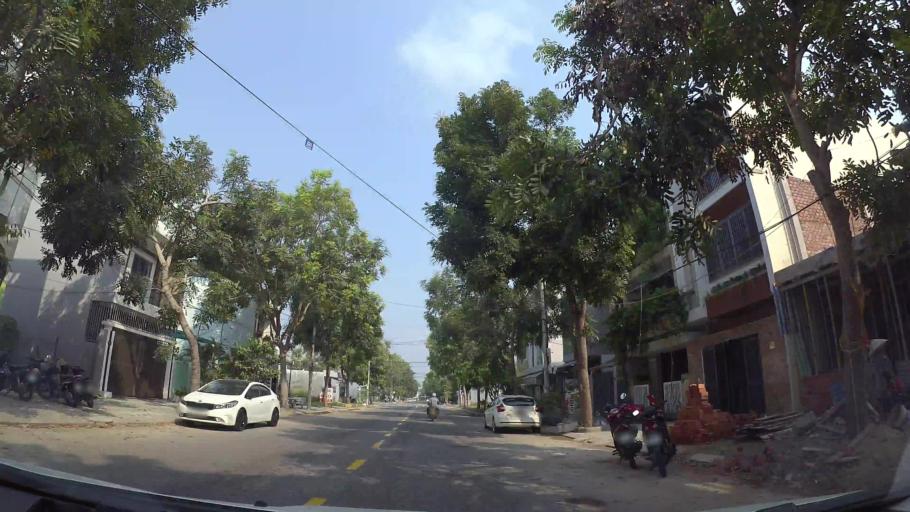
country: VN
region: Da Nang
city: Ngu Hanh Son
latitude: 16.0310
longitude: 108.2413
